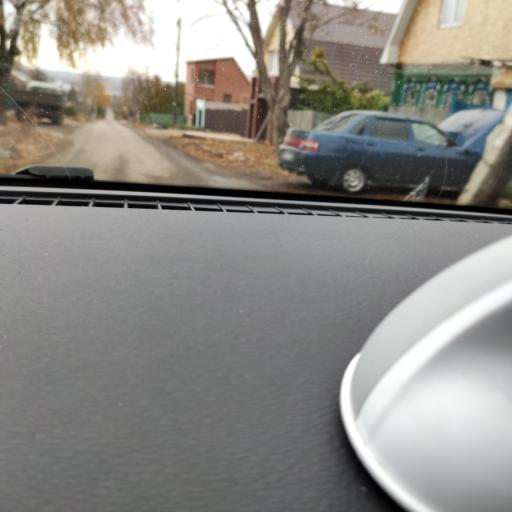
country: RU
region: Samara
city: Samara
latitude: 53.1834
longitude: 50.1867
